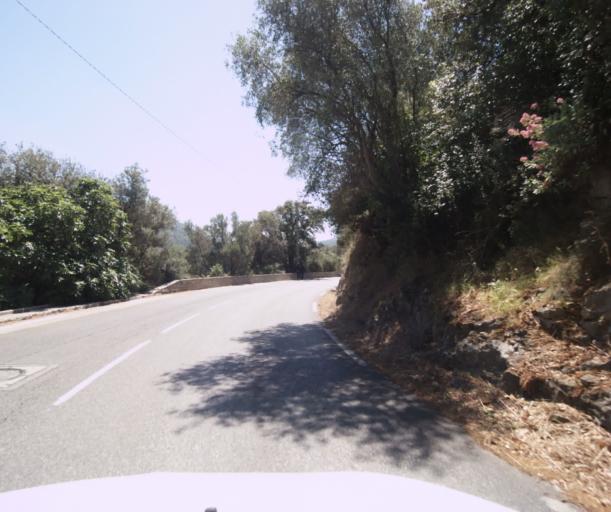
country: FR
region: Provence-Alpes-Cote d'Azur
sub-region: Departement du Var
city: Le Revest-les-Eaux
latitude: 43.1753
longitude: 5.9252
